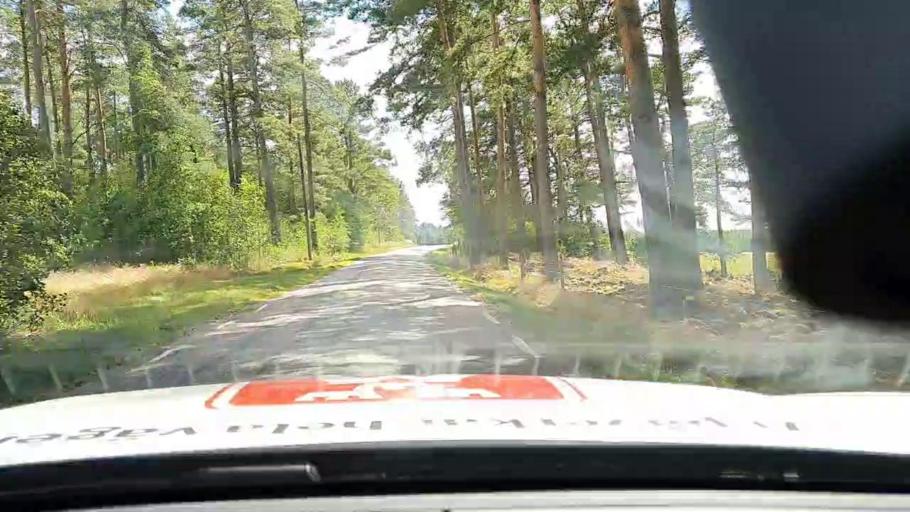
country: SE
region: Vaestra Goetaland
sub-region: Toreboda Kommun
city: Toereboda
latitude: 58.5756
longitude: 14.1239
